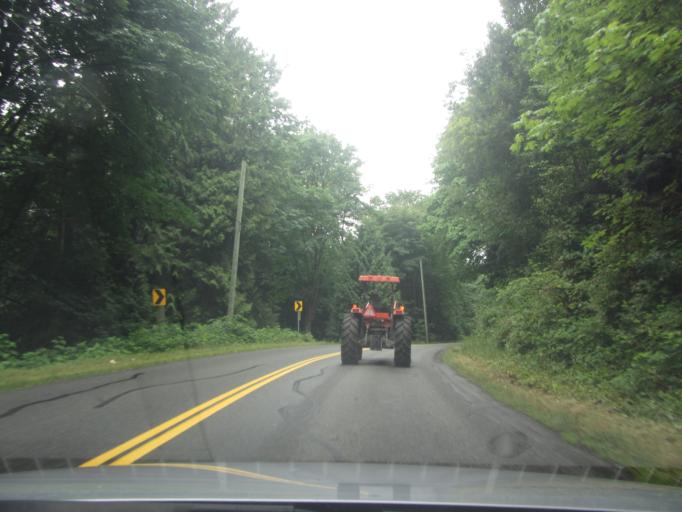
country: CA
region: British Columbia
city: Abbotsford
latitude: 49.1029
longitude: -122.3576
